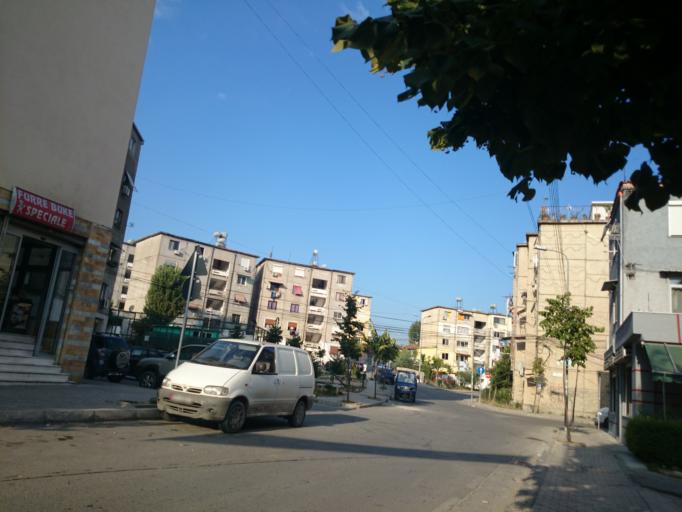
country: AL
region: Tirane
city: Tirana
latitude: 41.3199
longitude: 19.7930
